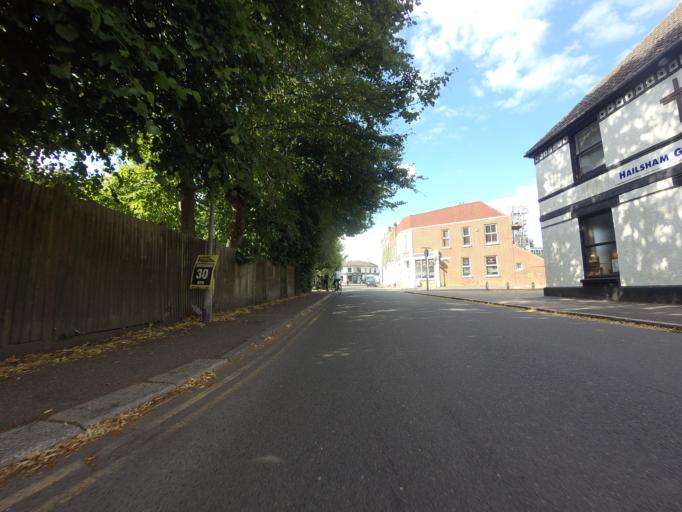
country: GB
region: England
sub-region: East Sussex
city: Hailsham
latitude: 50.8609
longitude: 0.2575
